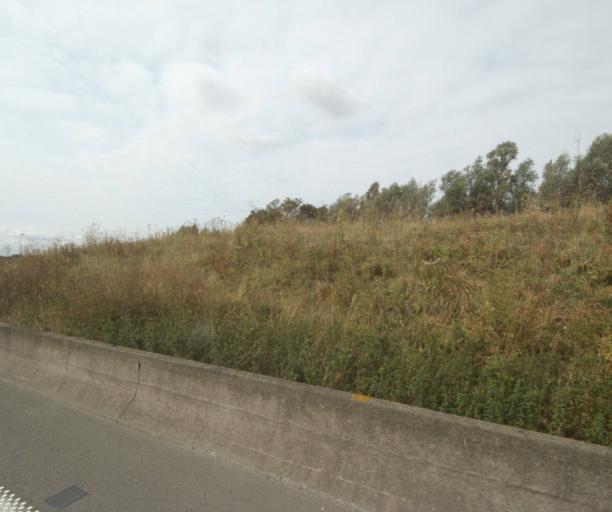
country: FR
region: Nord-Pas-de-Calais
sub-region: Departement du Nord
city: Lezennes
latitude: 50.6021
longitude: 3.1286
